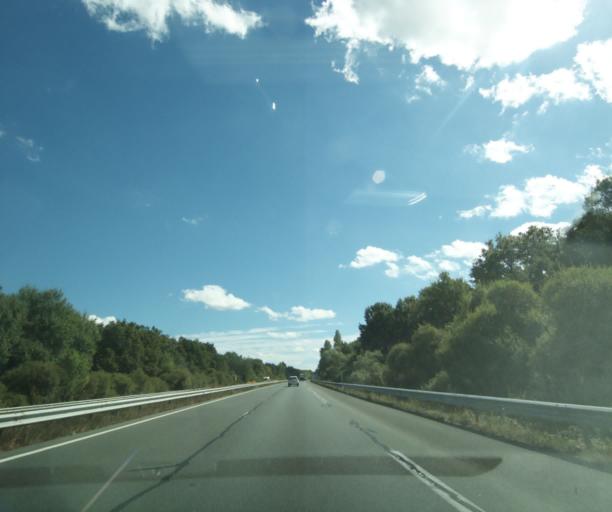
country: FR
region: Aquitaine
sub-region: Departement du Lot-et-Garonne
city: Fourques-sur-Garonne
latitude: 44.4181
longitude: 0.1741
